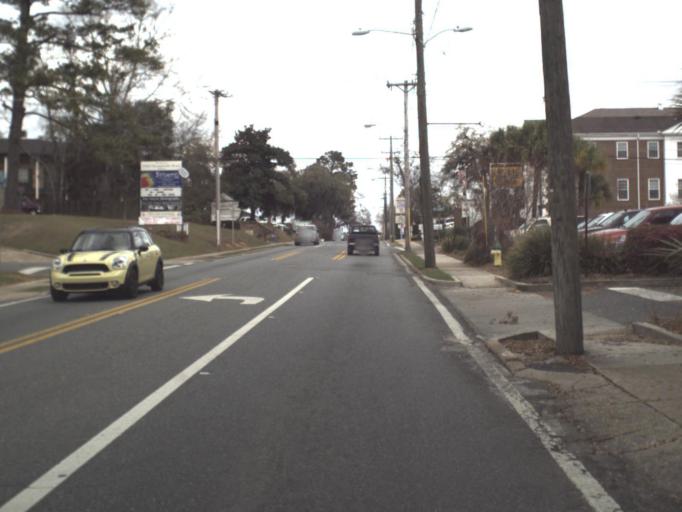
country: US
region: Florida
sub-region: Leon County
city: Tallahassee
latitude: 30.4522
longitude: -84.2792
